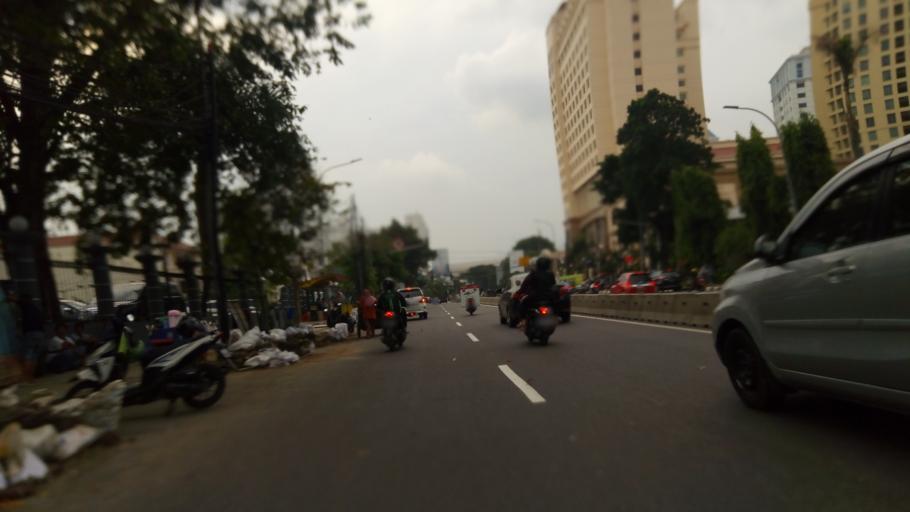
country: ID
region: Jakarta Raya
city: Jakarta
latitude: -6.1758
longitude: 106.8396
